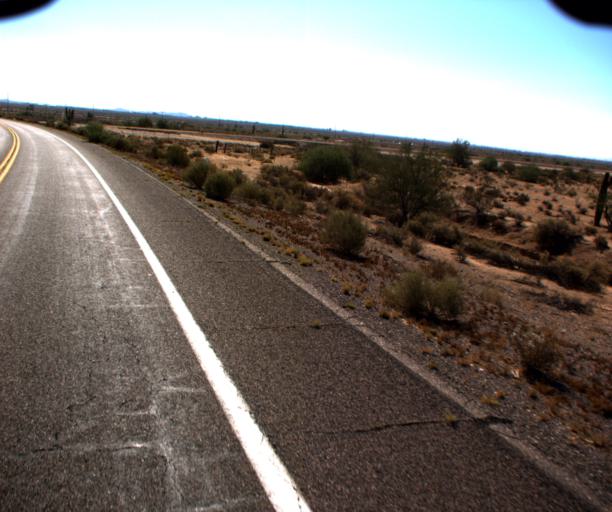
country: US
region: Arizona
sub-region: Pinal County
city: Blackwater
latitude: 33.0192
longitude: -111.6400
